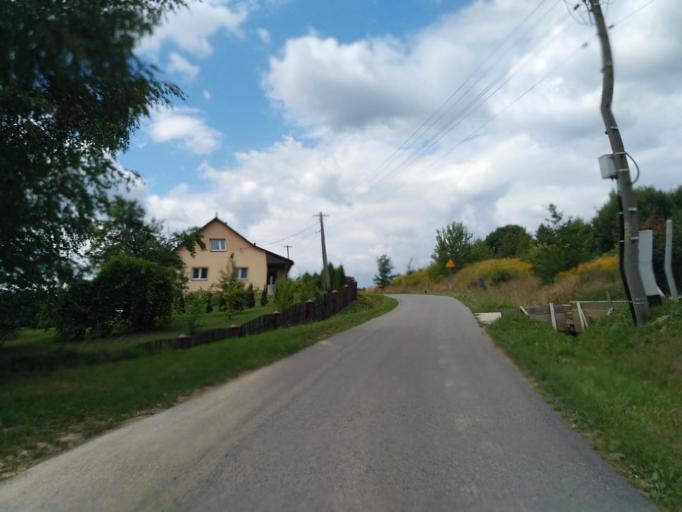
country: PL
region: Subcarpathian Voivodeship
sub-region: Powiat rzeszowski
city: Chmielnik
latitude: 49.9535
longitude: 22.1219
